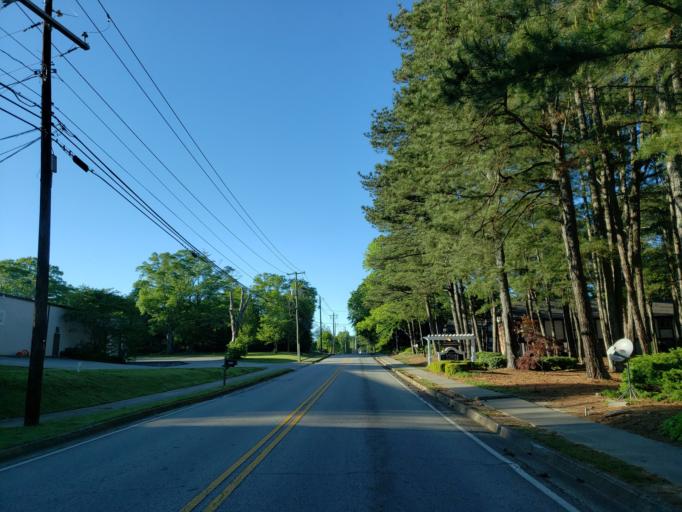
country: US
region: Georgia
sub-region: Cobb County
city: Fair Oaks
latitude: 33.9060
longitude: -84.5400
